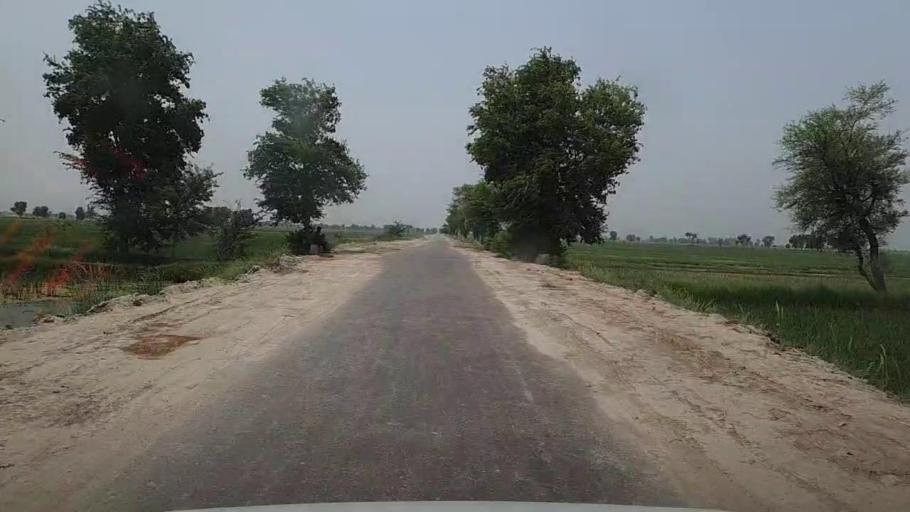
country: PK
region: Sindh
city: Sita Road
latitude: 27.0845
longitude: 67.9116
